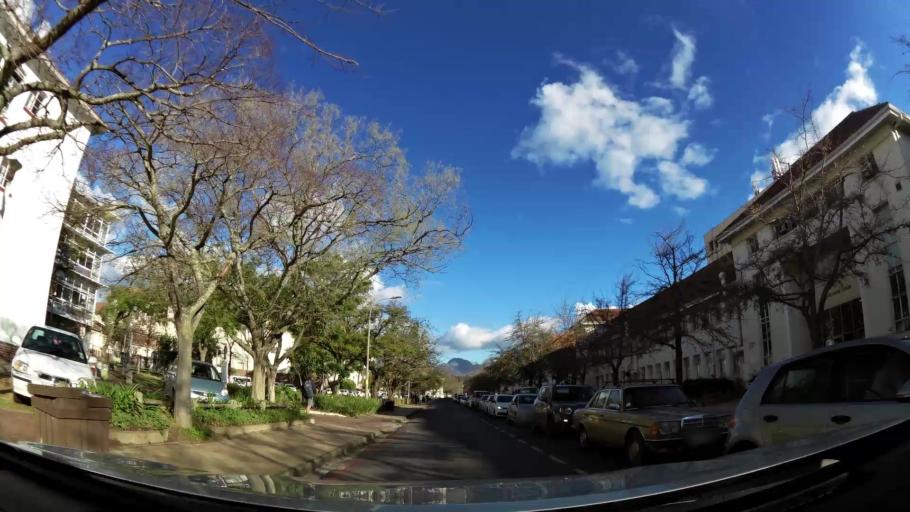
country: ZA
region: Western Cape
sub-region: Cape Winelands District Municipality
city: Stellenbosch
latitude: -33.9320
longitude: 18.8678
